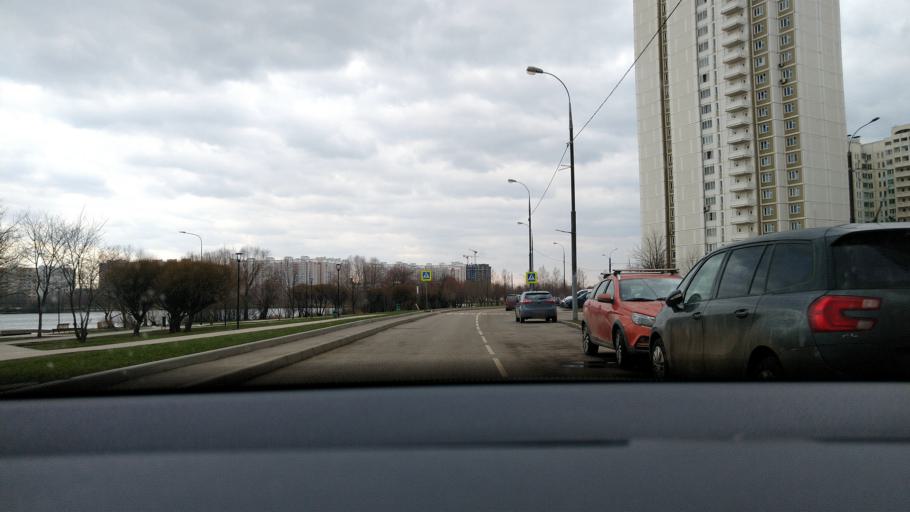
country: RU
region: Moskovskaya
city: Kommunarka
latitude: 55.5331
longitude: 37.5040
